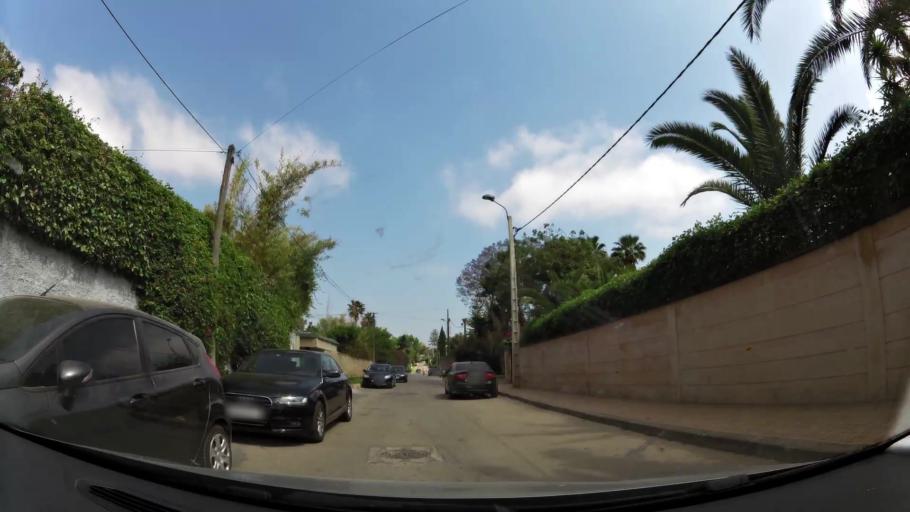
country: MA
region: Rabat-Sale-Zemmour-Zaer
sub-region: Rabat
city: Rabat
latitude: 33.9814
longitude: -6.8389
